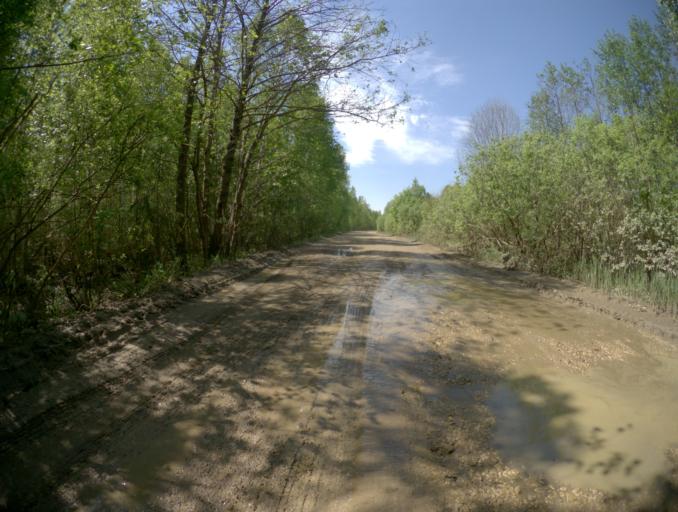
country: RU
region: Vladimir
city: Gusevskiy
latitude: 55.6924
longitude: 40.5429
